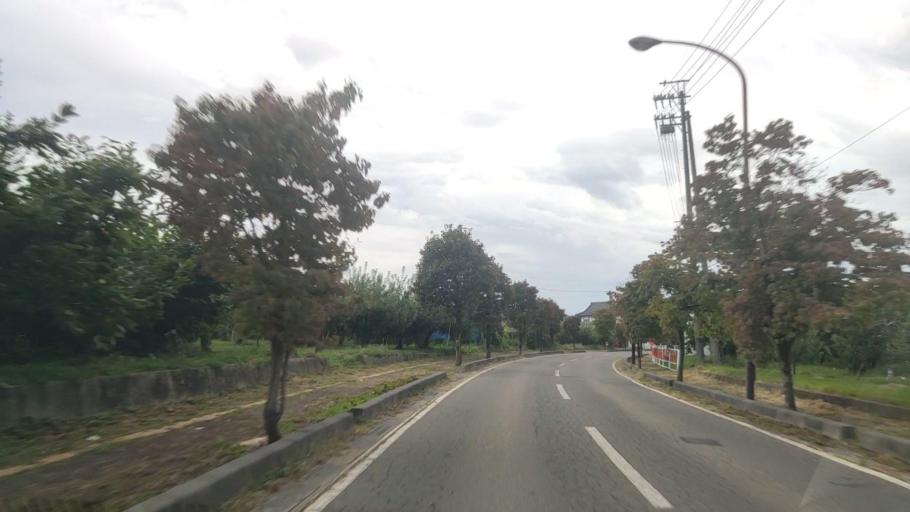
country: JP
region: Nagano
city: Nakano
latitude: 36.7831
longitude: 138.3562
